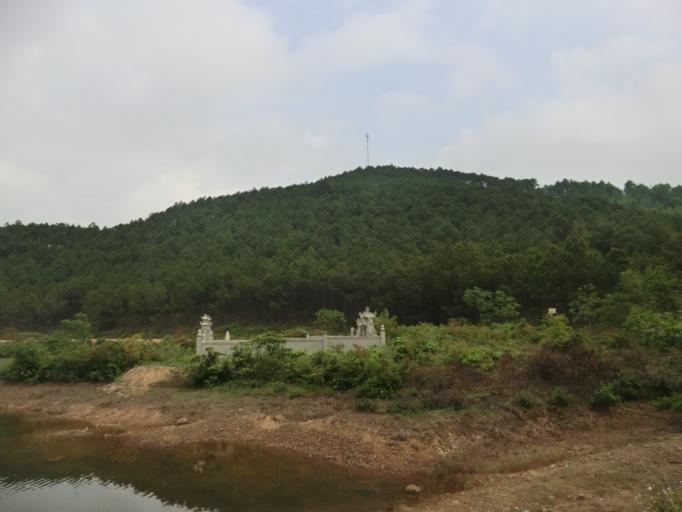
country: VN
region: Quang Binh
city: Ba Don
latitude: 17.6847
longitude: 106.4252
